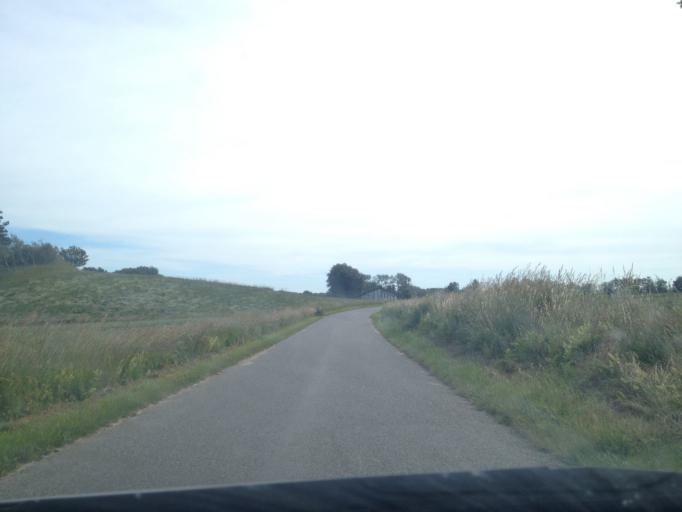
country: DK
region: Central Jutland
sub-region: Samso Kommune
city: Tranebjerg
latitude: 55.7905
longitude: 10.5559
